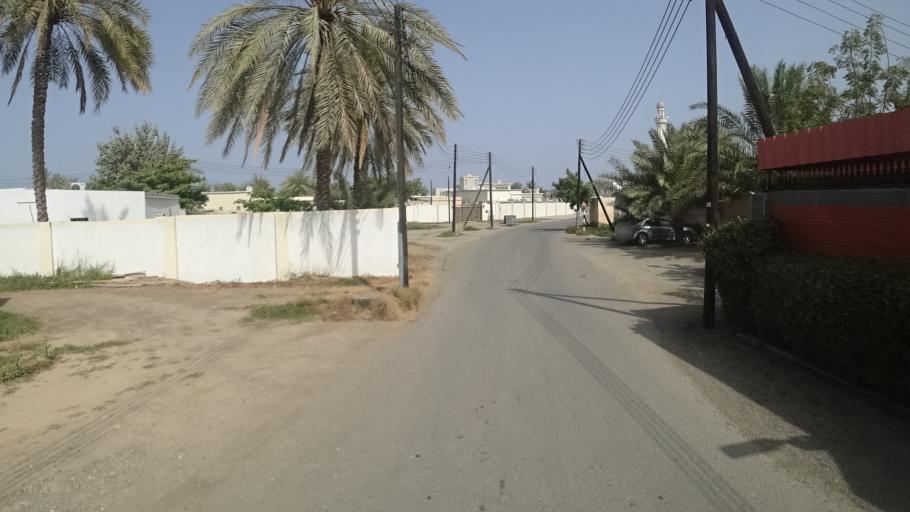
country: OM
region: Al Batinah
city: Saham
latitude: 24.2316
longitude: 56.8291
